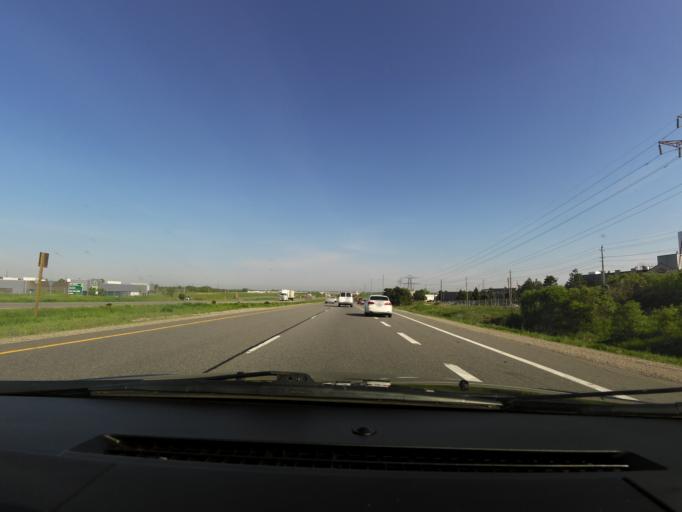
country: CA
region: Ontario
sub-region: Wellington County
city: Guelph
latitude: 43.4862
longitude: -80.2068
